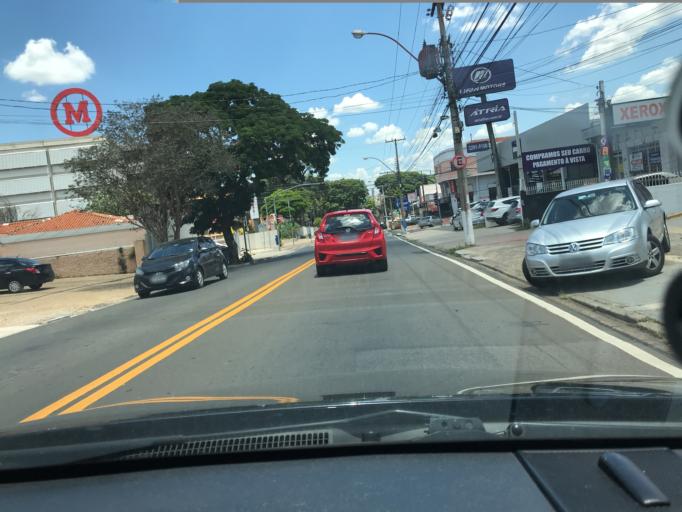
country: BR
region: Sao Paulo
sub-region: Campinas
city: Campinas
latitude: -22.8851
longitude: -47.0695
